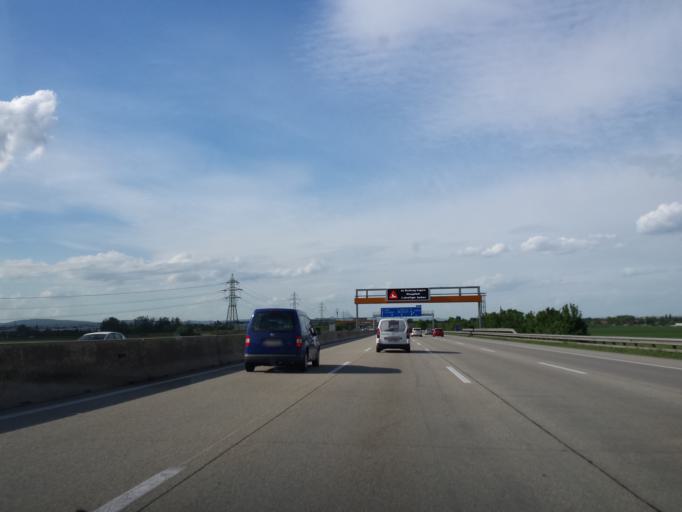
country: AT
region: Lower Austria
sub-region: Politischer Bezirk Modling
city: Laxenburg
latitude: 48.0493
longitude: 16.3419
